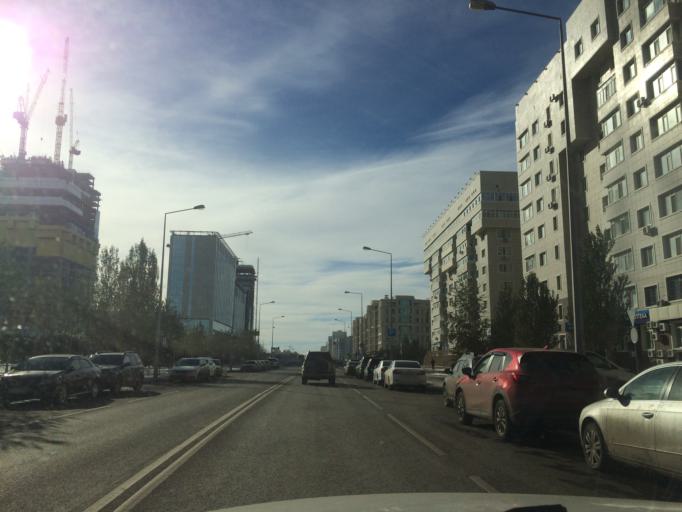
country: KZ
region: Astana Qalasy
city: Astana
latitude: 51.1252
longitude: 71.4272
